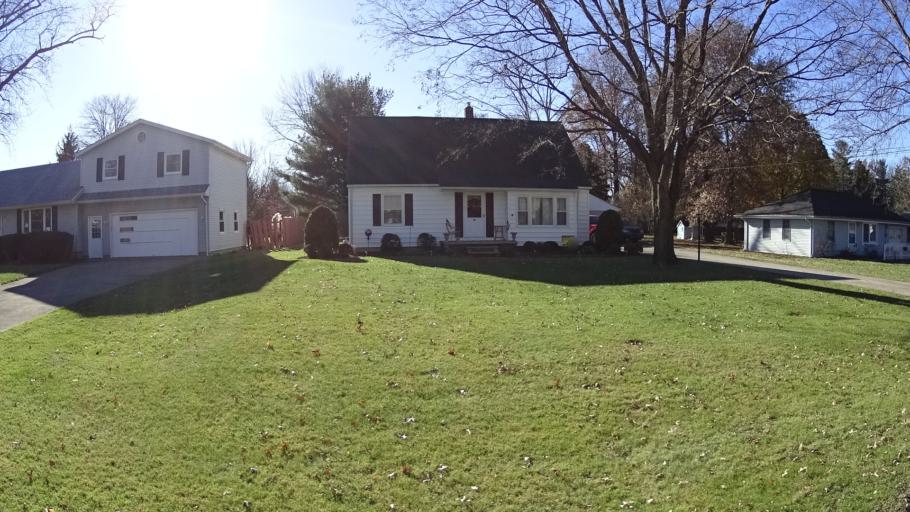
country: US
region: Ohio
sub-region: Lorain County
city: Avon
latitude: 41.4469
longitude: -82.0295
